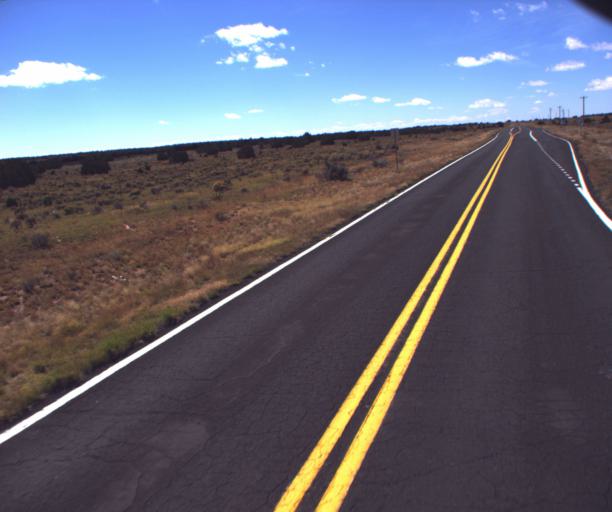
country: US
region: New Mexico
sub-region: McKinley County
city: Zuni Pueblo
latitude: 34.9678
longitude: -109.1465
